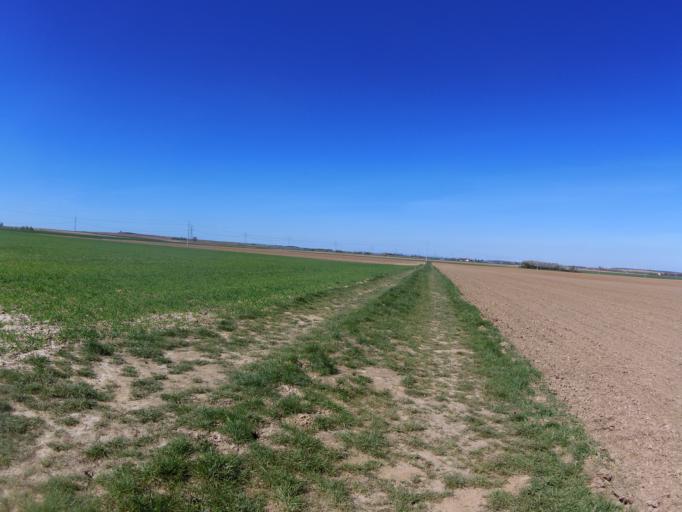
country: DE
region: Bavaria
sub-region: Regierungsbezirk Unterfranken
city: Biebelried
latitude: 49.8012
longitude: 10.0990
